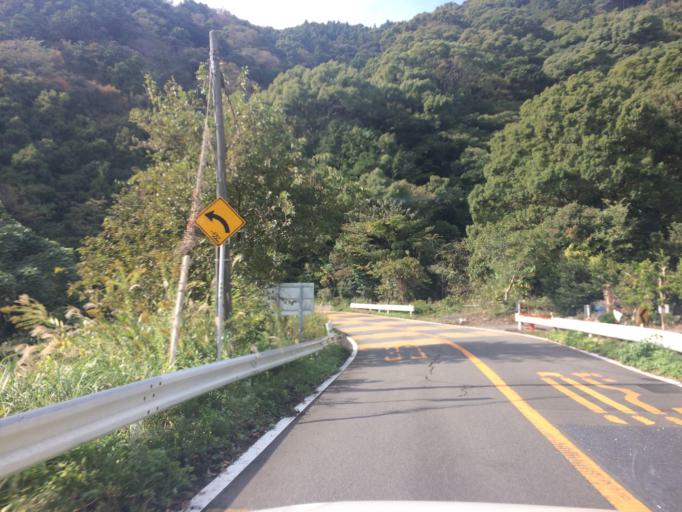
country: JP
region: Shizuoka
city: Yaizu
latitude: 34.9044
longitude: 138.3502
